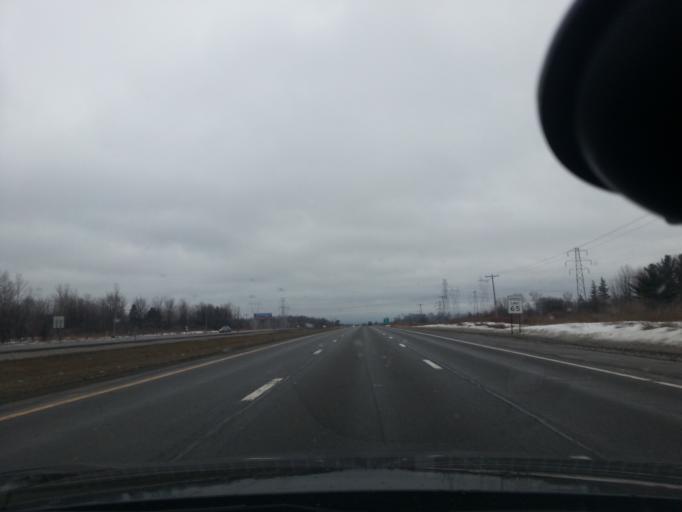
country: US
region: New York
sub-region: Onondaga County
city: Brewerton
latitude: 43.1966
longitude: -76.1239
